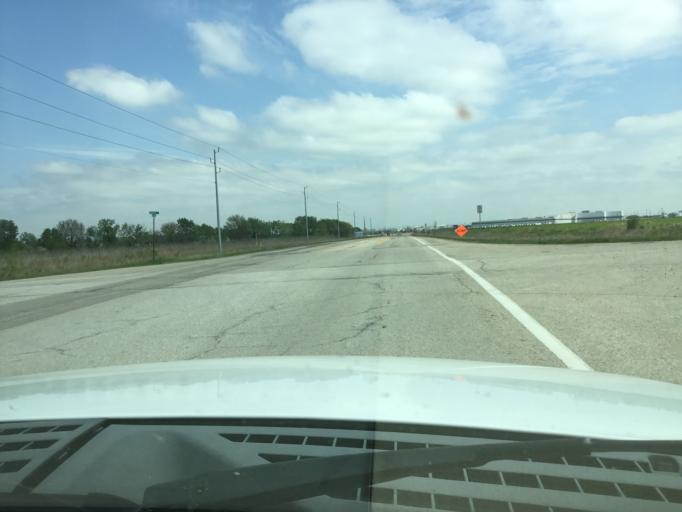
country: US
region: Kansas
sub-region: Osage County
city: Carbondale
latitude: 38.9297
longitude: -95.7060
